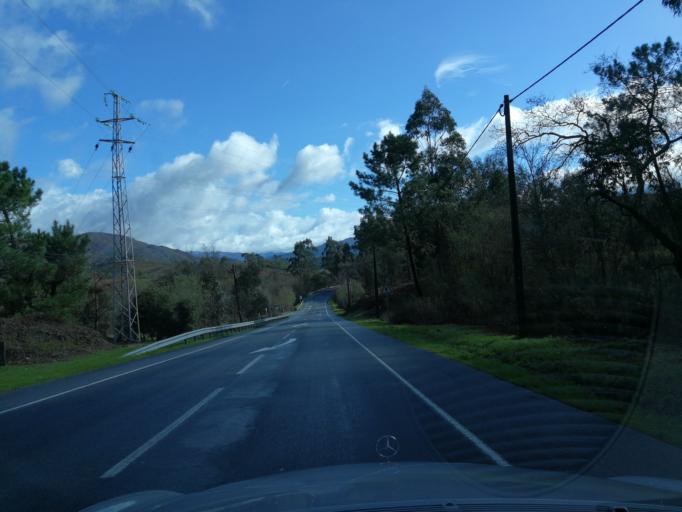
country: PT
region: Viana do Castelo
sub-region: Ponte da Barca
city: Ponte da Barca
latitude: 41.8104
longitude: -8.3499
